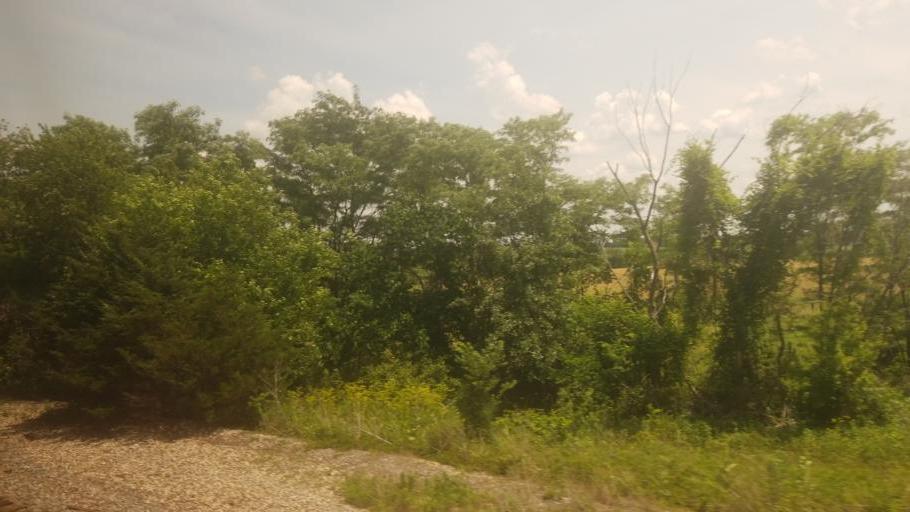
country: US
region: Missouri
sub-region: Macon County
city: La Plata
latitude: 40.0979
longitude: -92.4130
